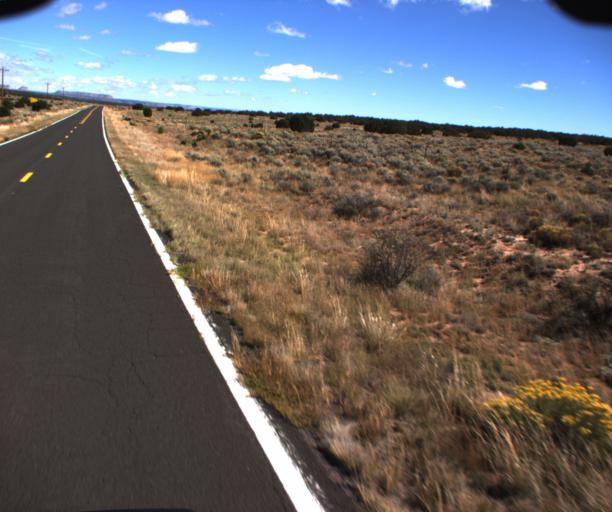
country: US
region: New Mexico
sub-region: McKinley County
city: Zuni Pueblo
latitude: 35.0033
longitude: -109.0839
